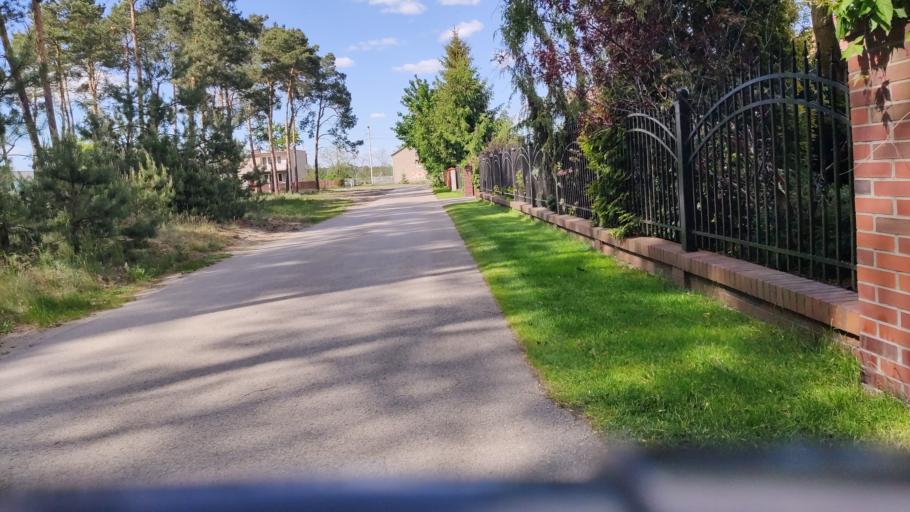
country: PL
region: Kujawsko-Pomorskie
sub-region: Wloclawek
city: Wloclawek
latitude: 52.6022
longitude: 19.0812
